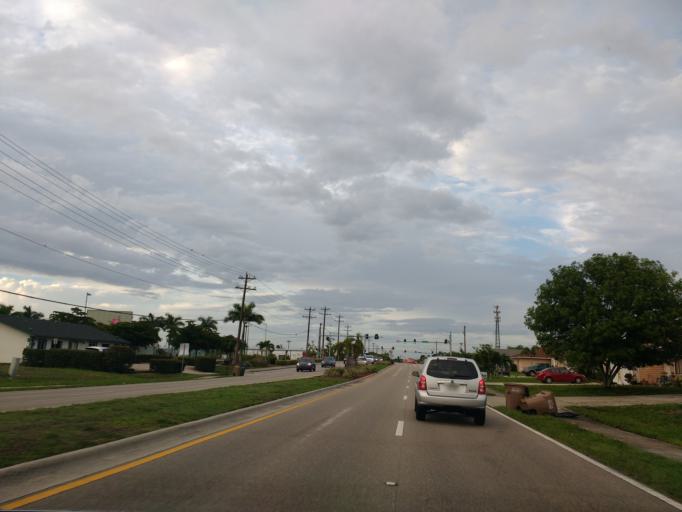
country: US
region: Florida
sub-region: Lee County
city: Lochmoor Waterway Estates
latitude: 26.6316
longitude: -81.9548
